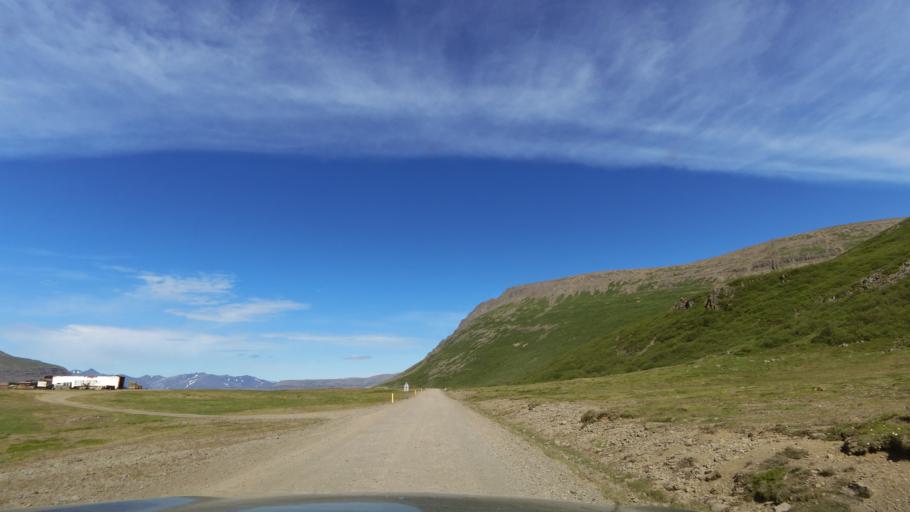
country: IS
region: Westfjords
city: Isafjoerdur
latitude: 65.6034
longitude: -23.5344
